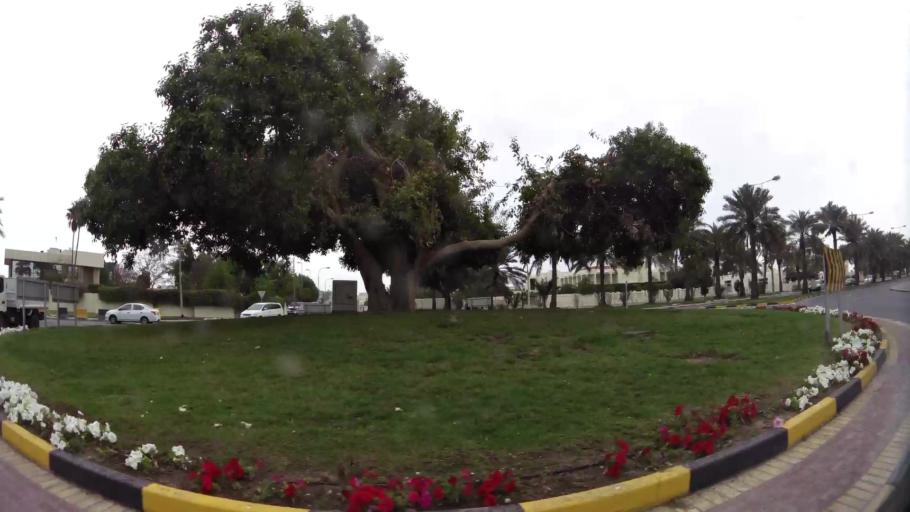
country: BH
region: Northern
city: Ar Rifa'
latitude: 26.1214
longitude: 50.5360
